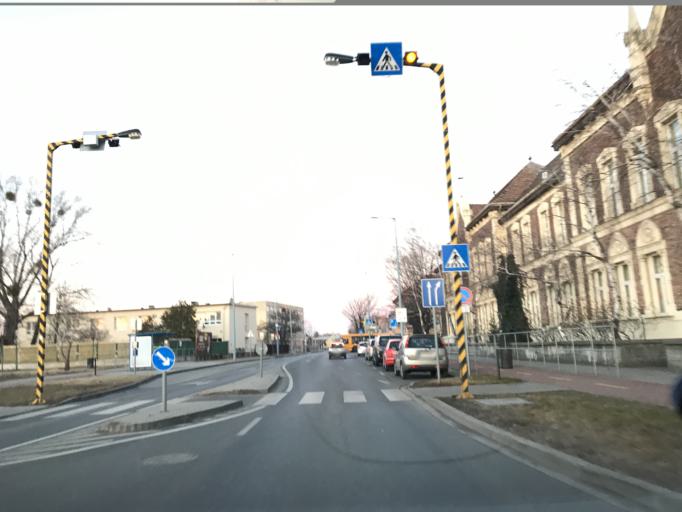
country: HU
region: Gyor-Moson-Sopron
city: Gyor
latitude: 47.6864
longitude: 17.6531
